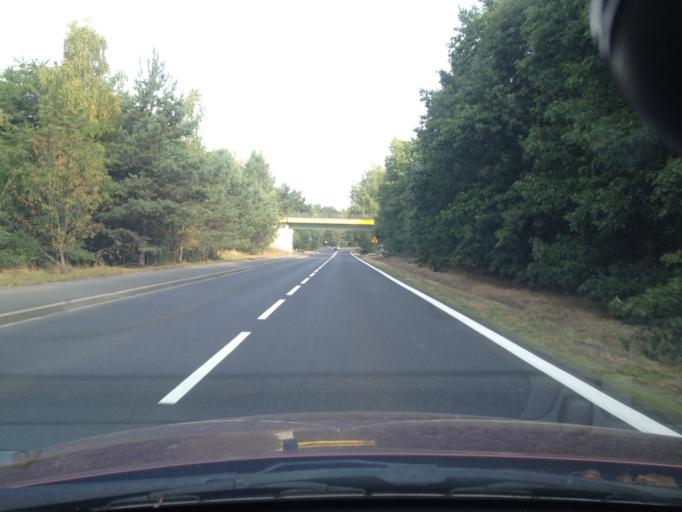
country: PL
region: Lubusz
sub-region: Powiat zaganski
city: Szprotawa
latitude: 51.4418
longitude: 15.6004
